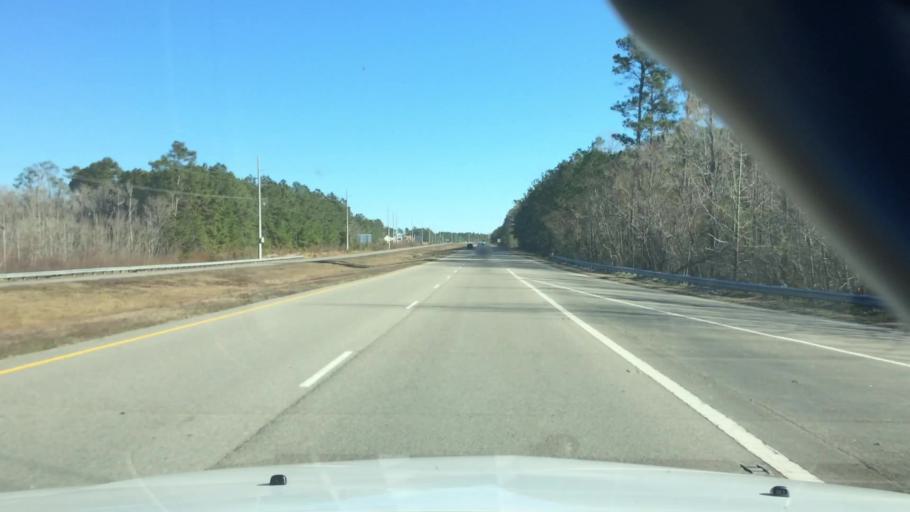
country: US
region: North Carolina
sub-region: Brunswick County
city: Shallotte
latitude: 33.9788
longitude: -78.4014
